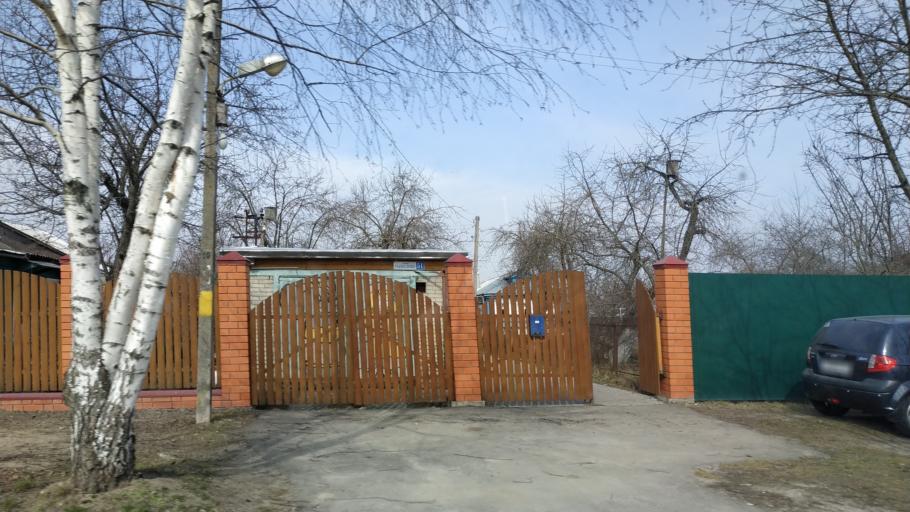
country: RU
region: Moskovskaya
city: Beloozerskiy
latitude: 55.4024
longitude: 38.3785
